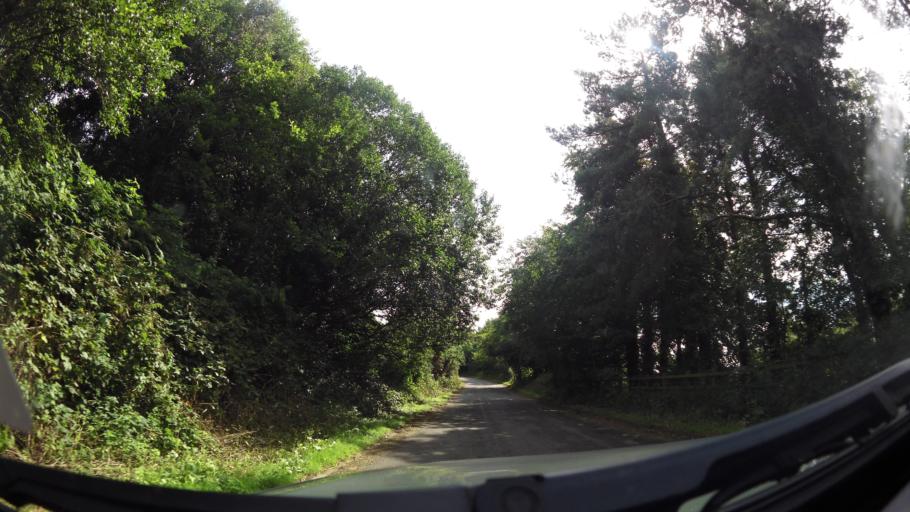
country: GB
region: Wales
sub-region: Caerphilly County Borough
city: Abertridwr
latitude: 51.5756
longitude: -3.2876
